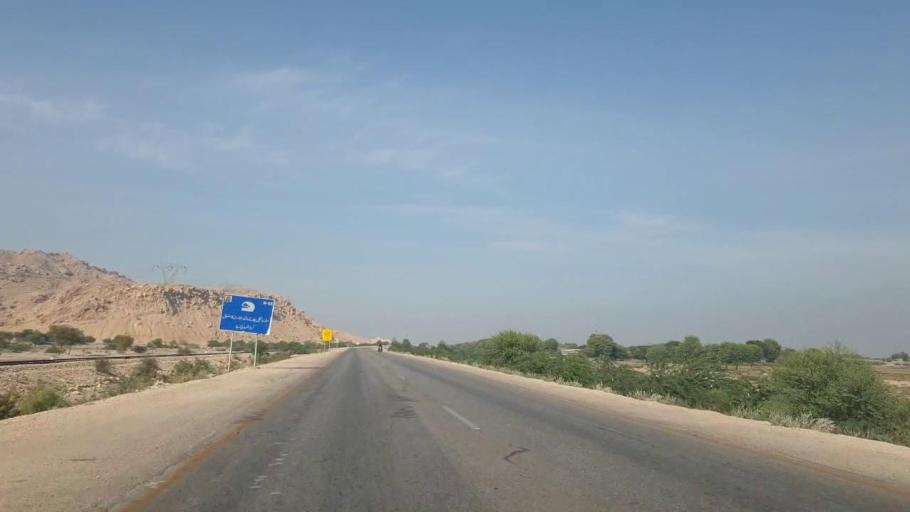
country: PK
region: Sindh
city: Sehwan
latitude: 26.2880
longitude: 67.8945
